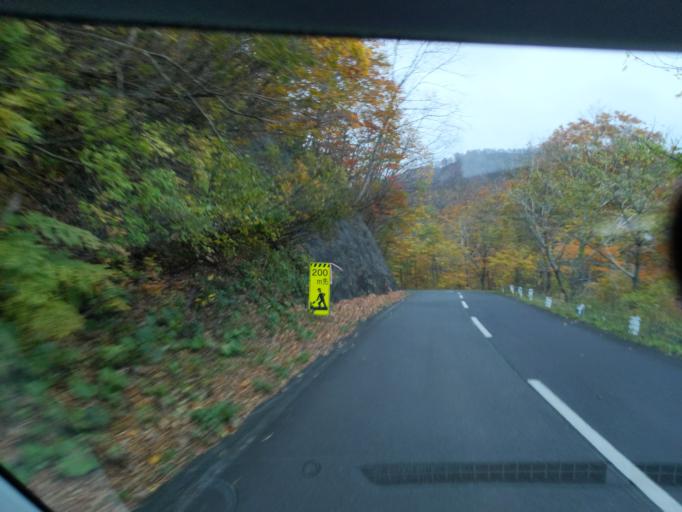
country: JP
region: Iwate
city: Mizusawa
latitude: 39.1110
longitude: 140.8560
